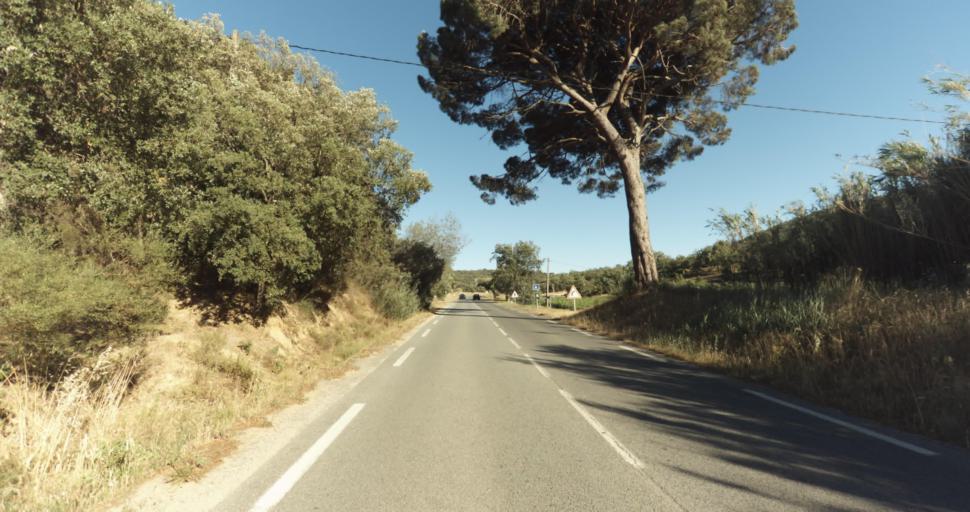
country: FR
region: Provence-Alpes-Cote d'Azur
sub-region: Departement du Var
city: Ramatuelle
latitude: 43.2372
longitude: 6.6084
